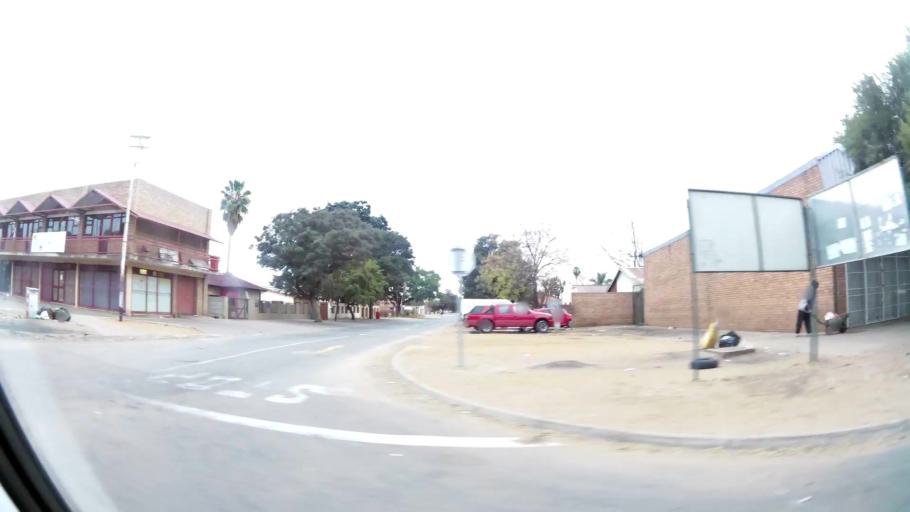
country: ZA
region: Limpopo
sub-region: Capricorn District Municipality
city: Polokwane
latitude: -23.9060
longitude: 29.4437
